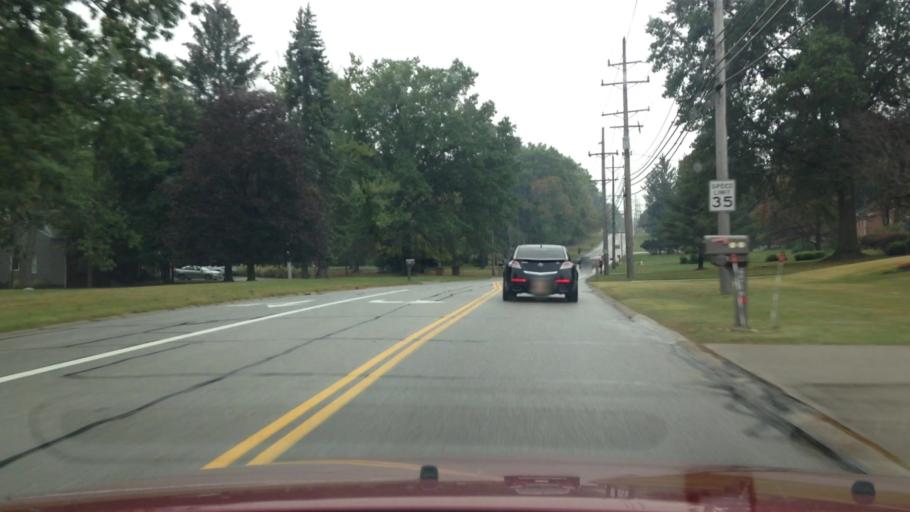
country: US
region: Ohio
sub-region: Cuyahoga County
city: Mayfield Heights
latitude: 41.5007
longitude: -81.4631
